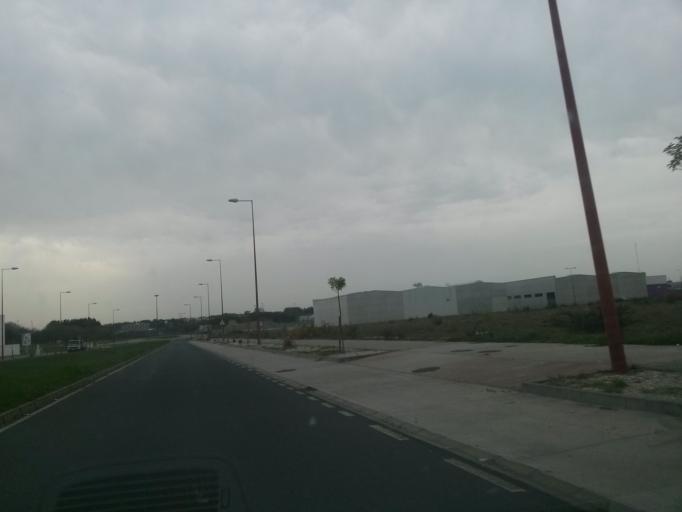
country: ES
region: Galicia
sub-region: Provincia de Lugo
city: Lugo
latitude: 43.0376
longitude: -7.5512
